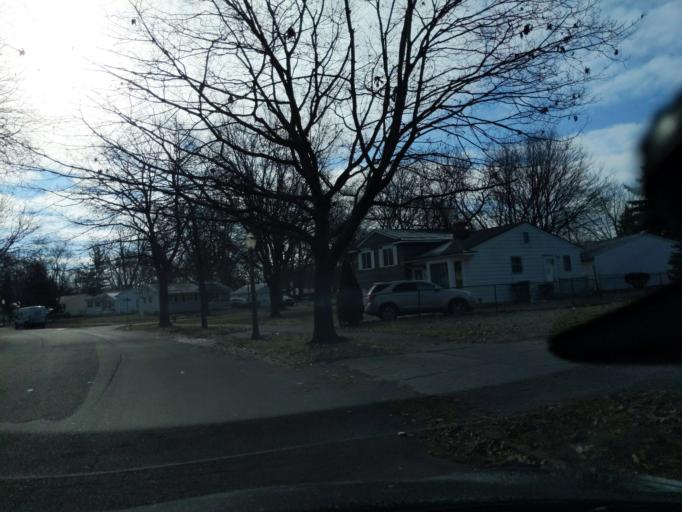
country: US
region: Michigan
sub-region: Eaton County
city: Waverly
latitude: 42.6943
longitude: -84.6022
